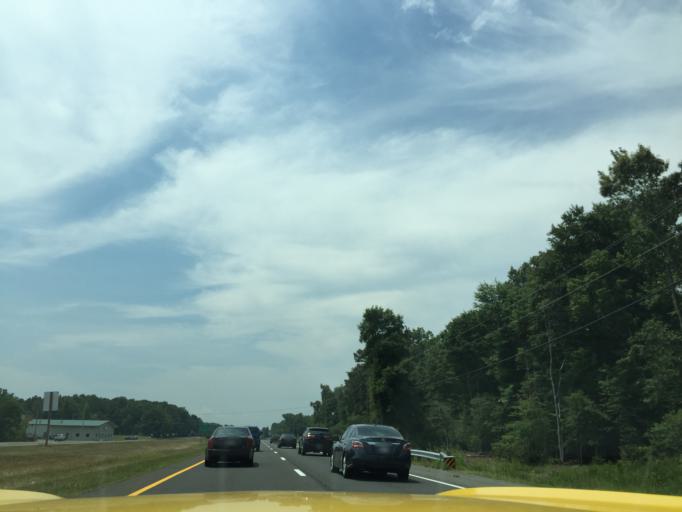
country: US
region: Maryland
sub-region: Prince George's County
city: Accokeek
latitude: 38.6521
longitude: -77.0332
